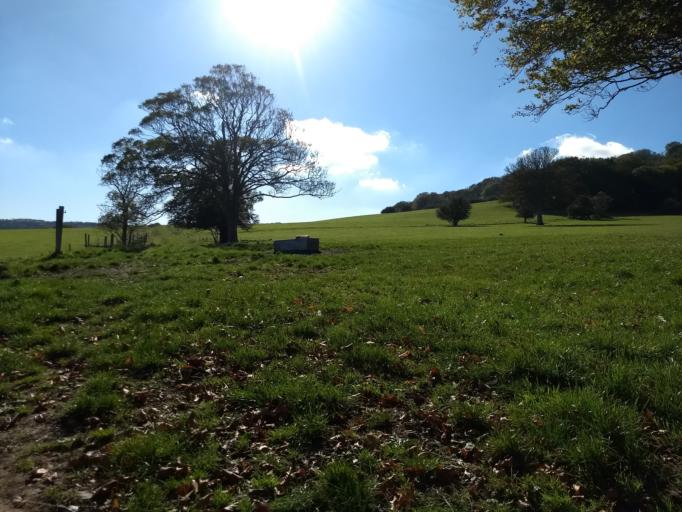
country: GB
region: England
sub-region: Isle of Wight
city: Ventnor
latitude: 50.6163
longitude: -1.2324
